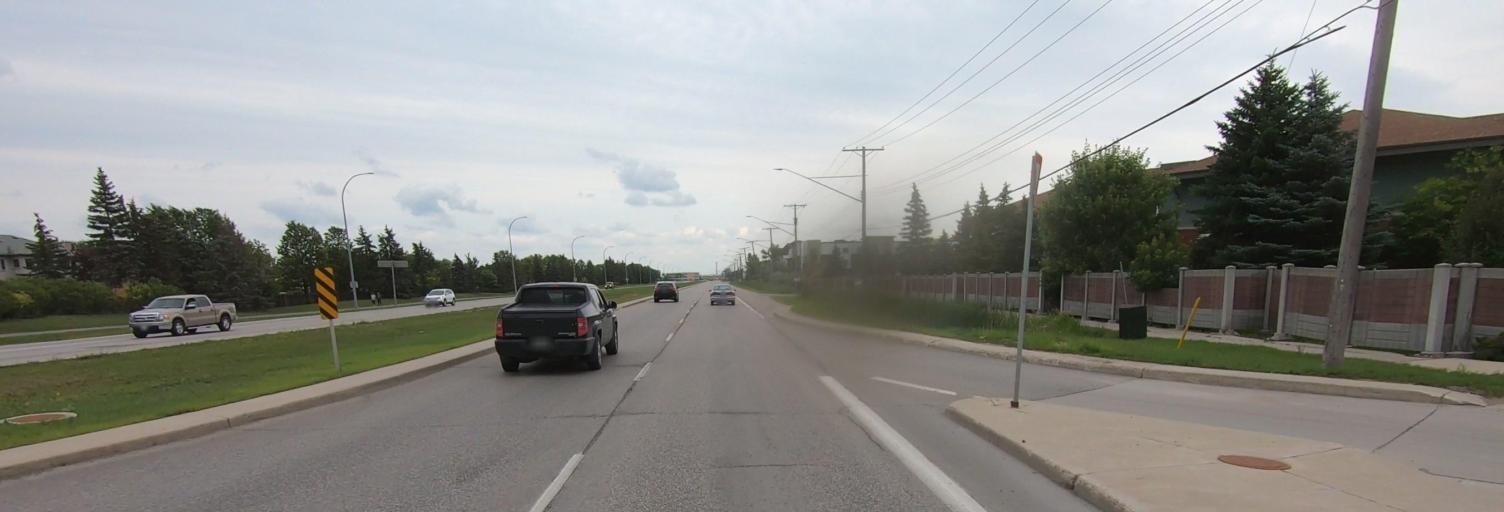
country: CA
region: Manitoba
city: Winnipeg
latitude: 49.8235
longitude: -97.1944
